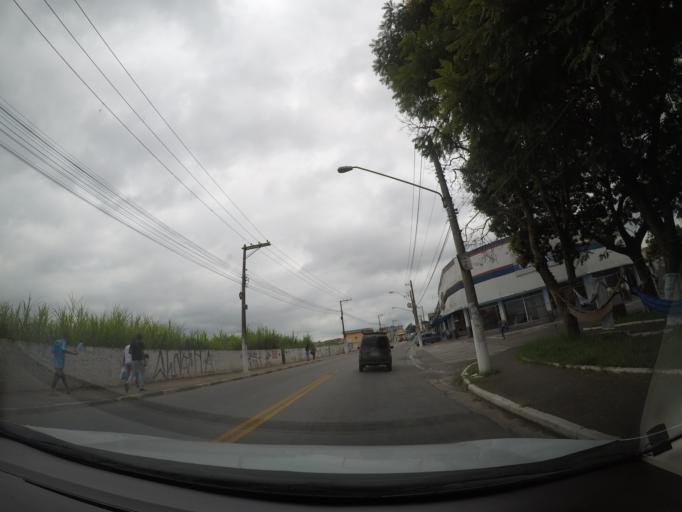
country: BR
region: Sao Paulo
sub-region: Itaquaquecetuba
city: Itaquaquecetuba
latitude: -23.4647
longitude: -46.4184
